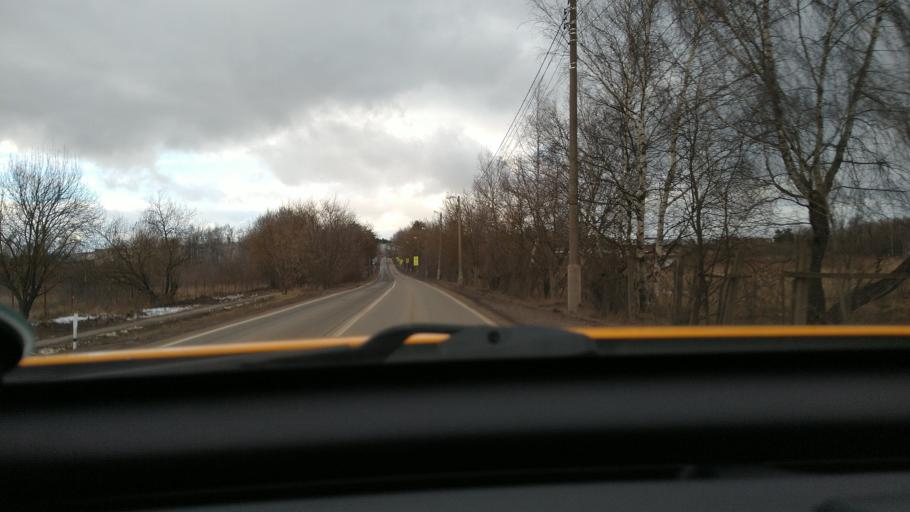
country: RU
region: Moskovskaya
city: Barvikha
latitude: 55.7626
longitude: 37.2280
